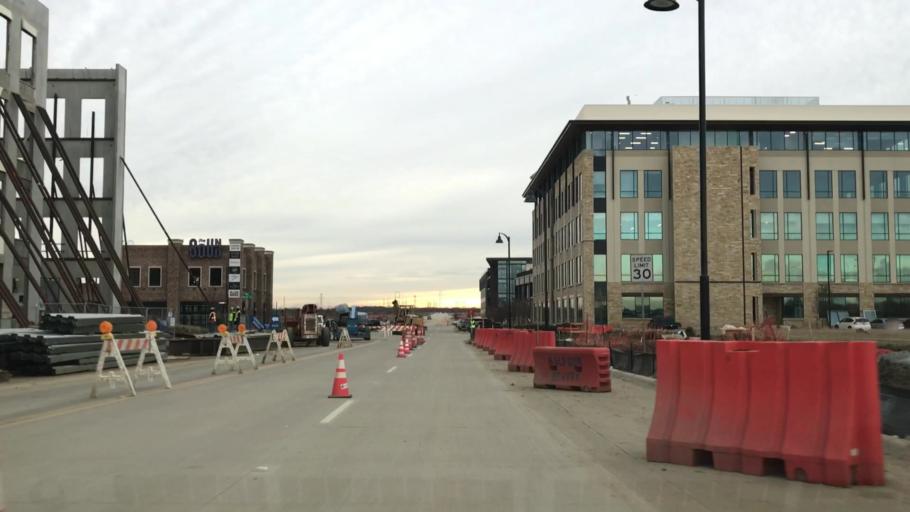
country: US
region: Texas
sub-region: Dallas County
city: Coppell
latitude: 32.9365
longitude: -96.9849
